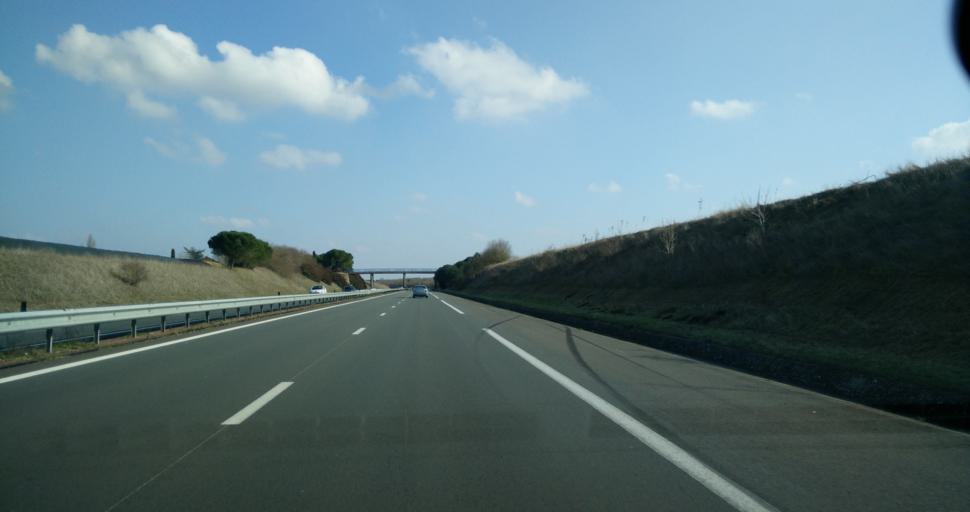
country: FR
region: Poitou-Charentes
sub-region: Departement de la Charente-Maritime
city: Saint-Jean-de-Liversay
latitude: 46.2249
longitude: -0.8635
